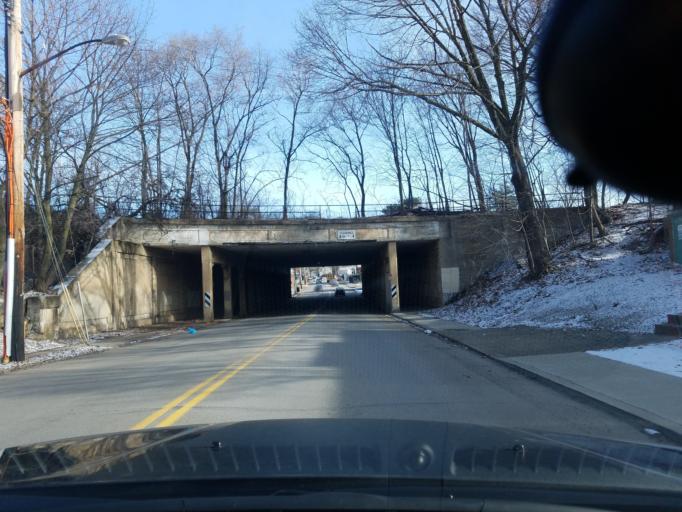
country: US
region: Pennsylvania
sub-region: Allegheny County
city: Wilkinsburg
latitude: 40.4497
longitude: -79.8932
